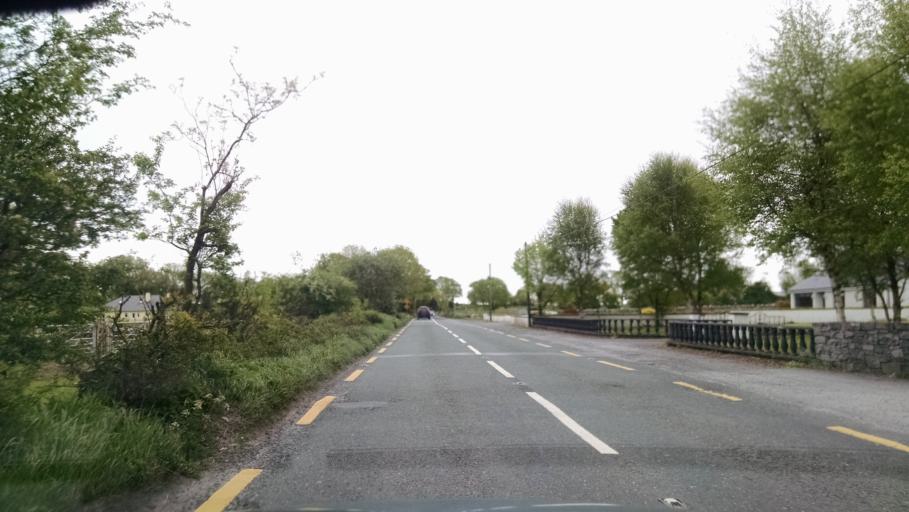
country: IE
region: Connaught
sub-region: County Galway
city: Claregalway
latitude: 53.4341
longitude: -9.0587
